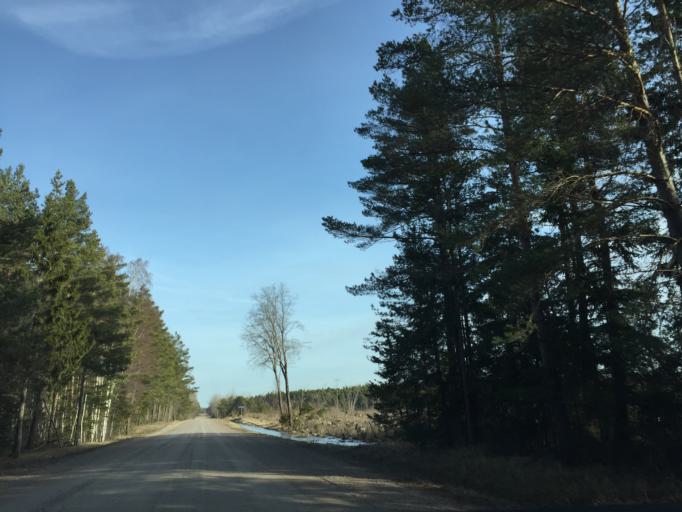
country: EE
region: Saare
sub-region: Kuressaare linn
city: Kuressaare
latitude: 58.3149
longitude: 21.9870
